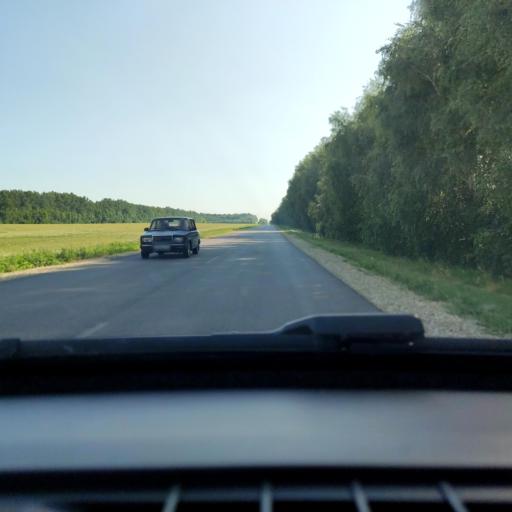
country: RU
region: Voronezj
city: Pereleshinskiy
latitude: 51.6410
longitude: 40.2870
